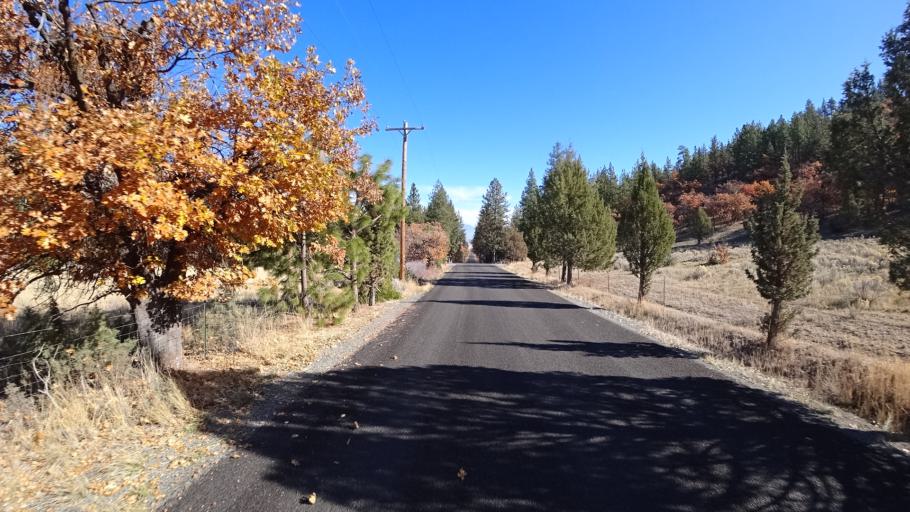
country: US
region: California
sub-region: Siskiyou County
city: Weed
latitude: 41.5034
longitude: -122.5841
